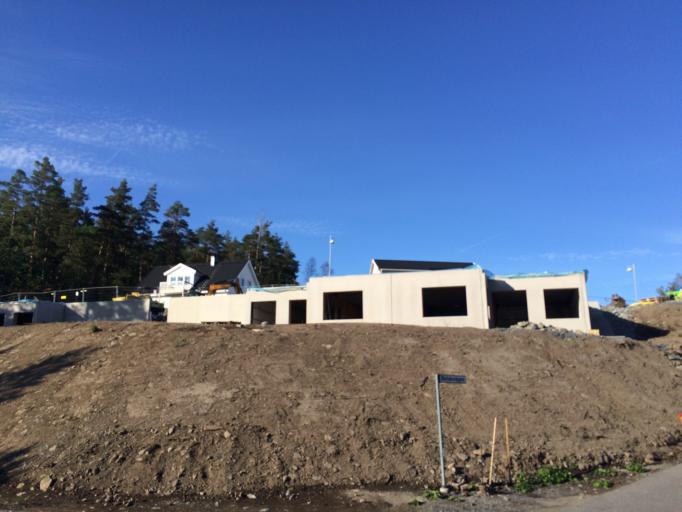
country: SE
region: Vaestra Goetaland
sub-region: Ale Kommun
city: Alafors
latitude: 57.9288
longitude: 12.0978
